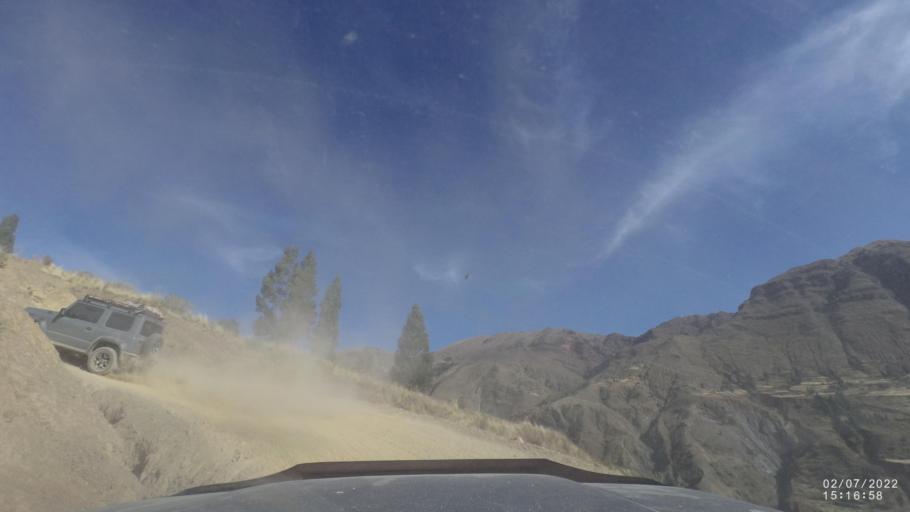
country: BO
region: Cochabamba
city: Irpa Irpa
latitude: -17.8660
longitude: -66.4328
